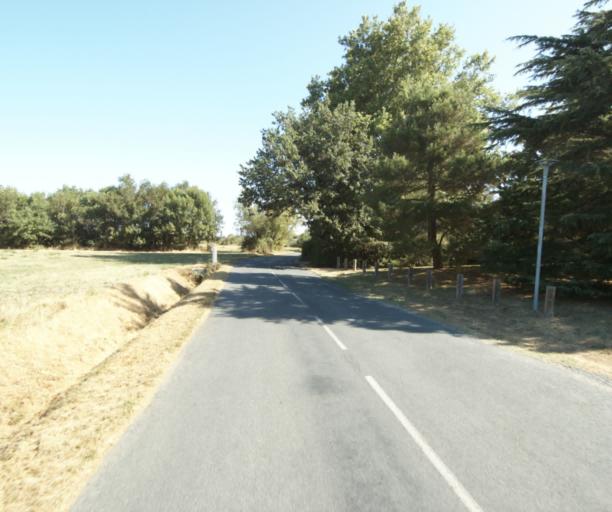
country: FR
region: Midi-Pyrenees
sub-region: Departement de la Haute-Garonne
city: Revel
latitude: 43.4653
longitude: 1.9896
